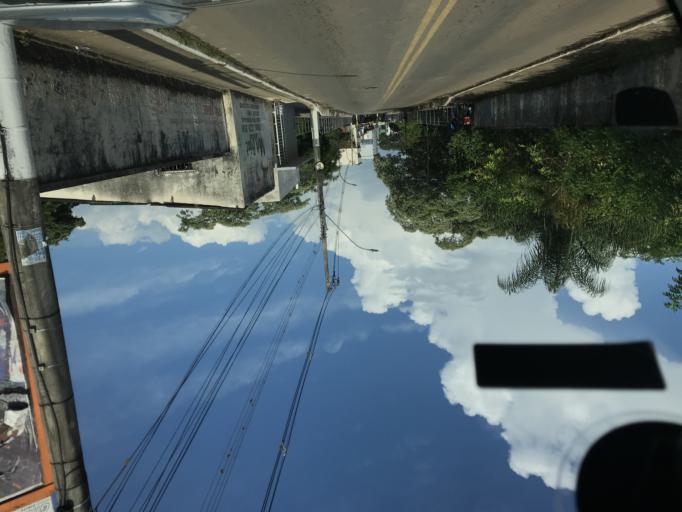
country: BR
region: Minas Gerais
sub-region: Tres Coracoes
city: Tres Coracoes
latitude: -21.7021
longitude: -45.2552
